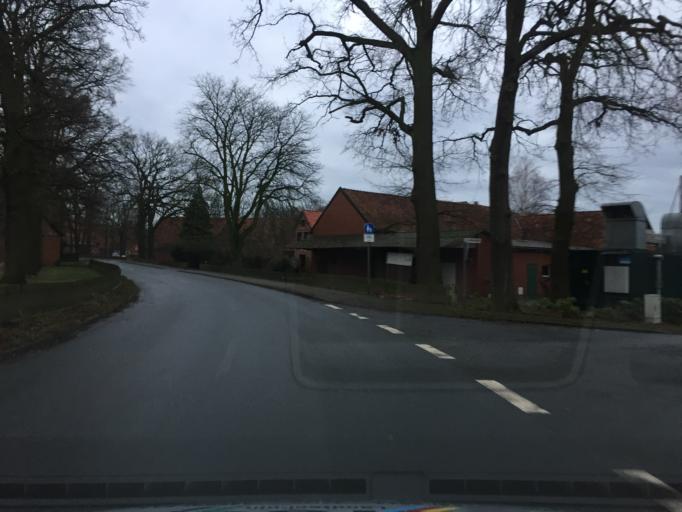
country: DE
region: Lower Saxony
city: Borstel
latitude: 52.6676
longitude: 8.9719
